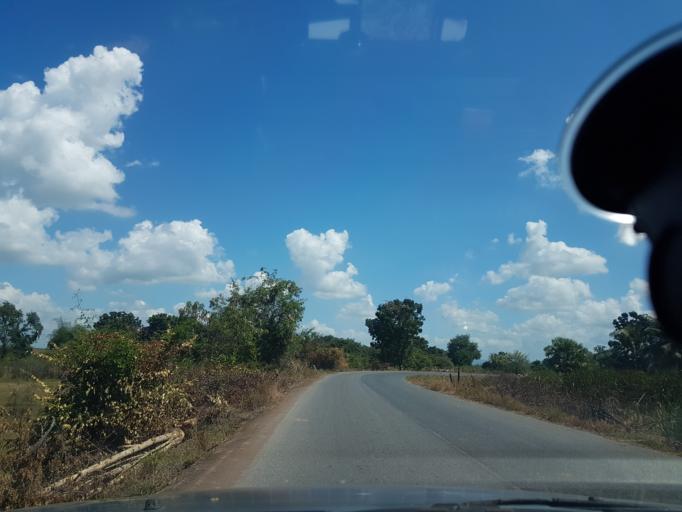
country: TH
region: Lop Buri
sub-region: Amphoe Tha Luang
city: Tha Luang
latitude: 14.9994
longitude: 101.0099
